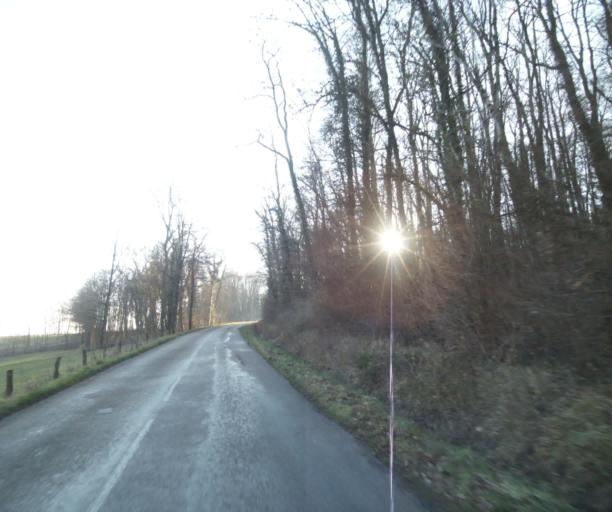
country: FR
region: Champagne-Ardenne
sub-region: Departement de la Haute-Marne
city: Bienville
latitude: 48.5748
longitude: 5.0803
